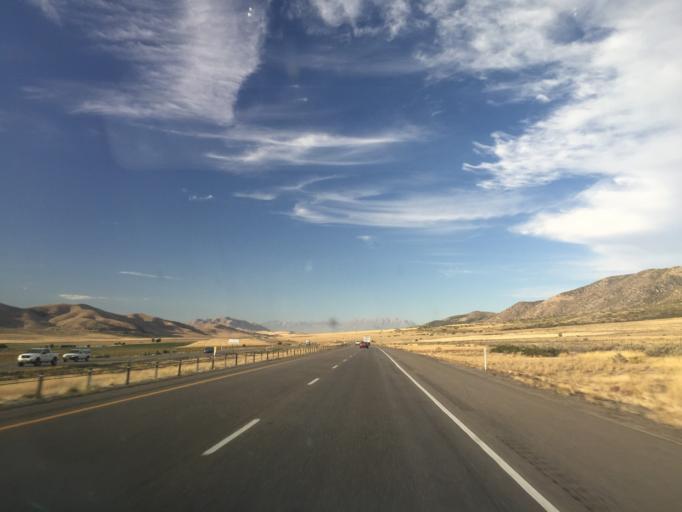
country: US
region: Utah
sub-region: Juab County
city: Mona
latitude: 39.8656
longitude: -111.8307
